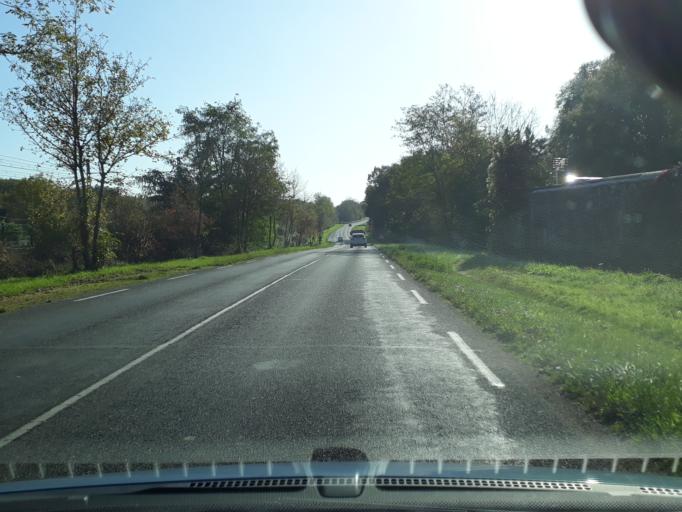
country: FR
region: Ile-de-France
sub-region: Departement de Seine-et-Marne
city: Livry-sur-Seine
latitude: 48.5070
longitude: 2.6810
